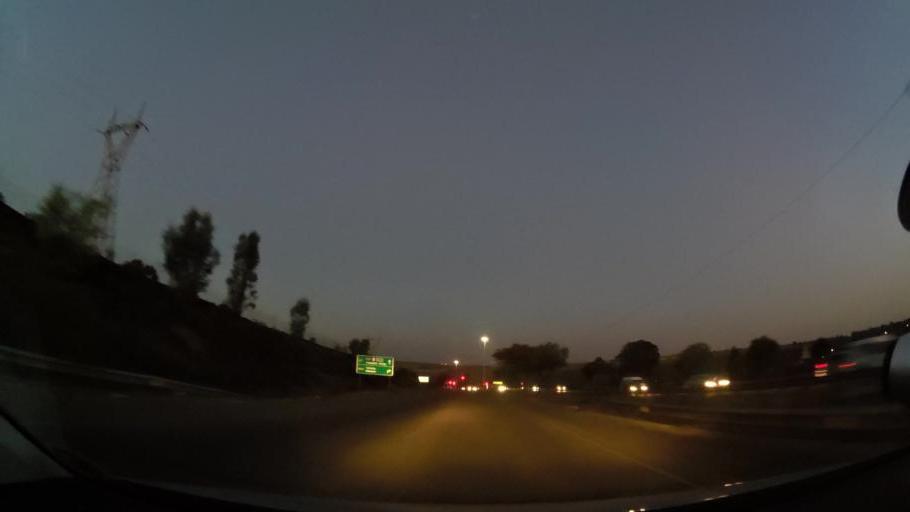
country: ZA
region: Gauteng
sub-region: City of Tshwane Metropolitan Municipality
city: Pretoria
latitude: -25.7775
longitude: 28.1685
